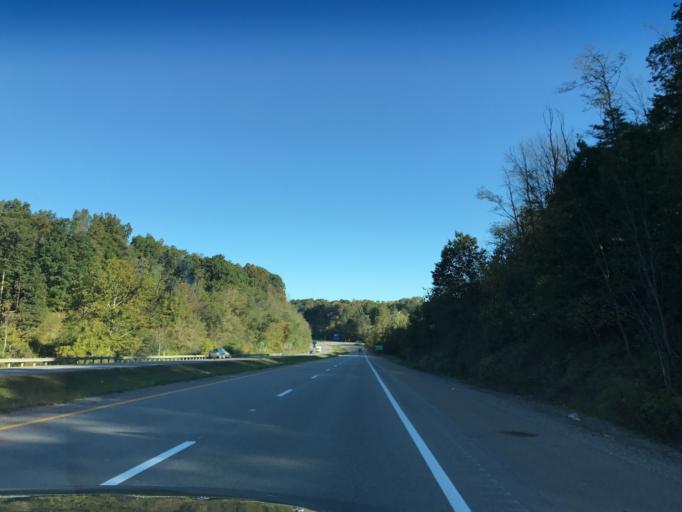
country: US
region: West Virginia
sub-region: Wood County
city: Parkersburg
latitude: 39.2566
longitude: -81.4842
